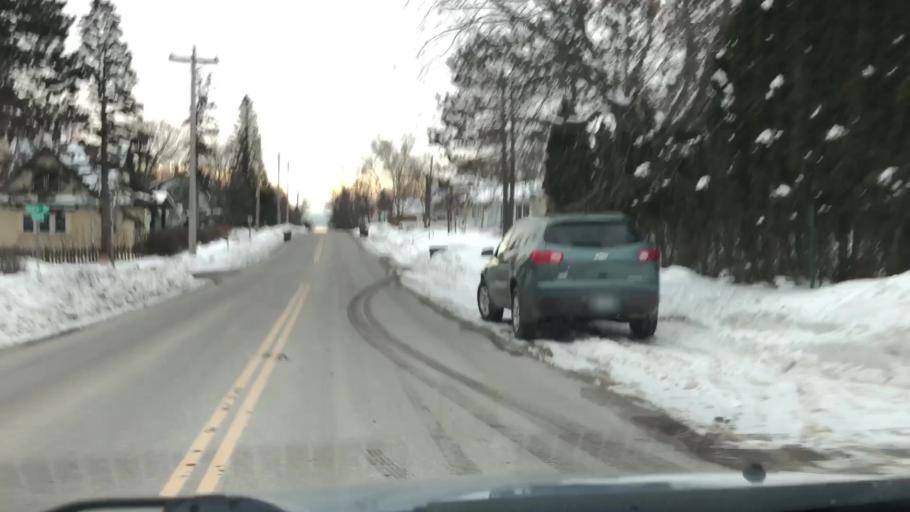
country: US
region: Minnesota
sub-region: Saint Louis County
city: Arnold
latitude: 46.8352
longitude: -92.0638
